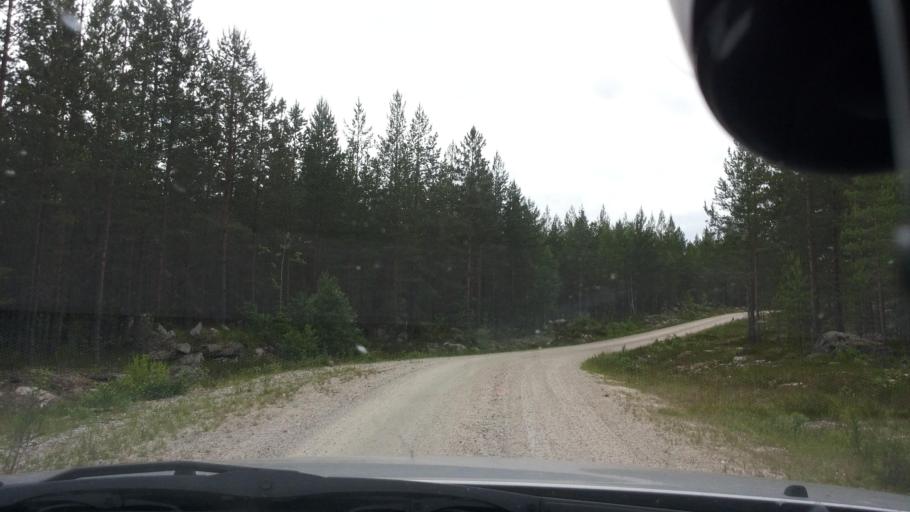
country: SE
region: Gaevleborg
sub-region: Ovanakers Kommun
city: Edsbyn
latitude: 61.4905
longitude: 15.3244
